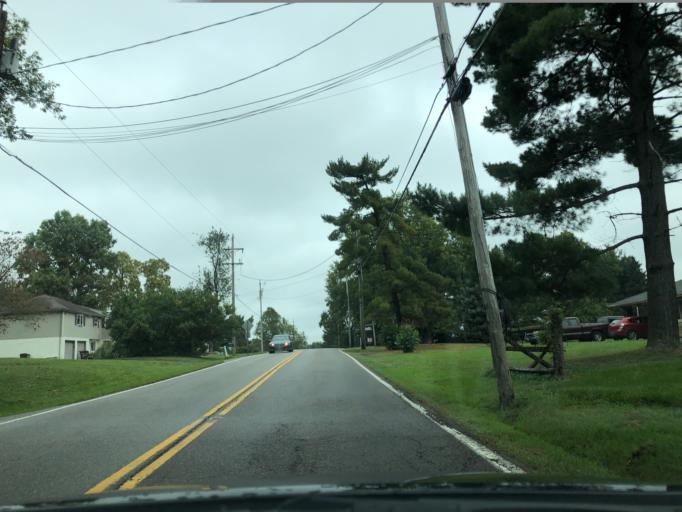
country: US
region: Ohio
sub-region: Hamilton County
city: Loveland
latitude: 39.2424
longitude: -84.2540
